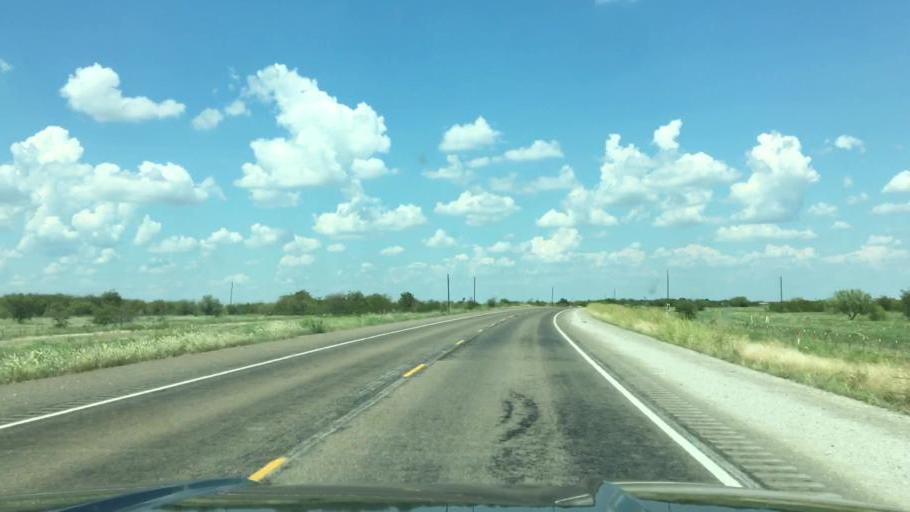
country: US
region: Texas
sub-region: Tarrant County
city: Haslet
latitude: 33.0065
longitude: -97.3417
